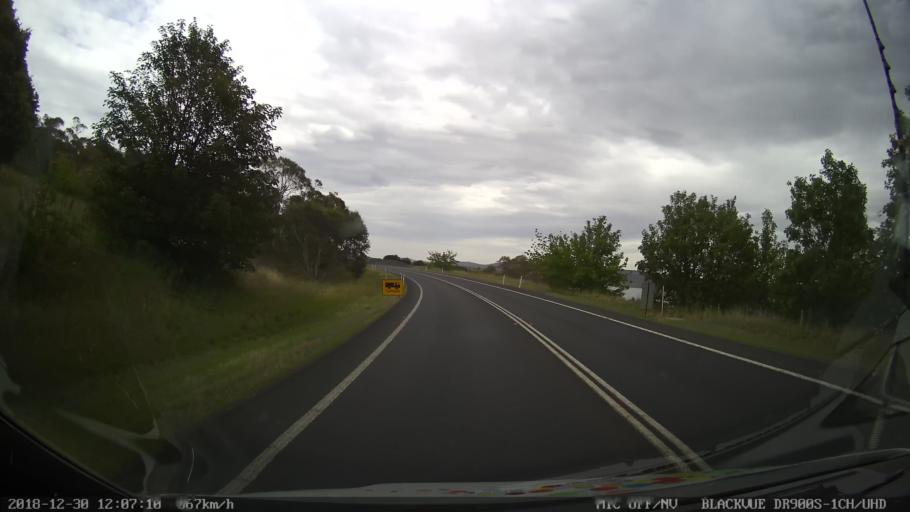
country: AU
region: New South Wales
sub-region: Snowy River
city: Jindabyne
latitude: -36.4074
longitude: 148.6002
